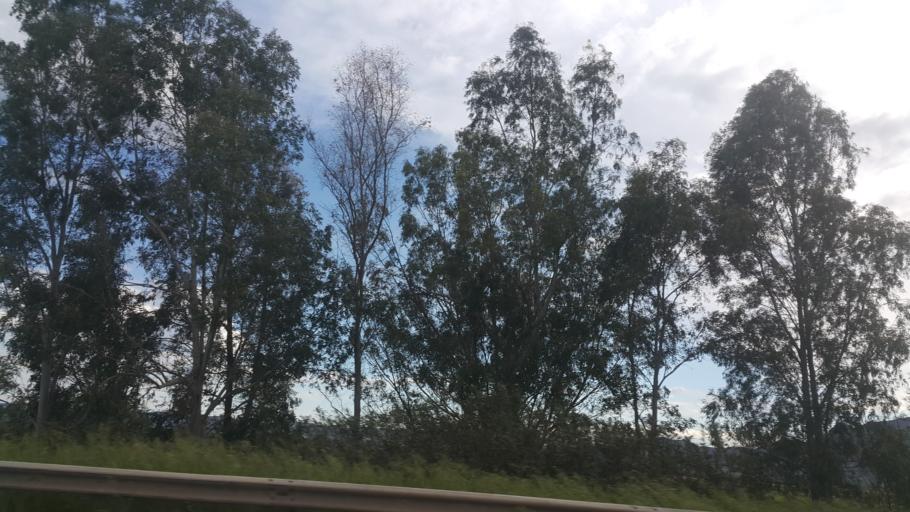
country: TR
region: Adana
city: Ceyhan
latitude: 36.9850
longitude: 35.7688
